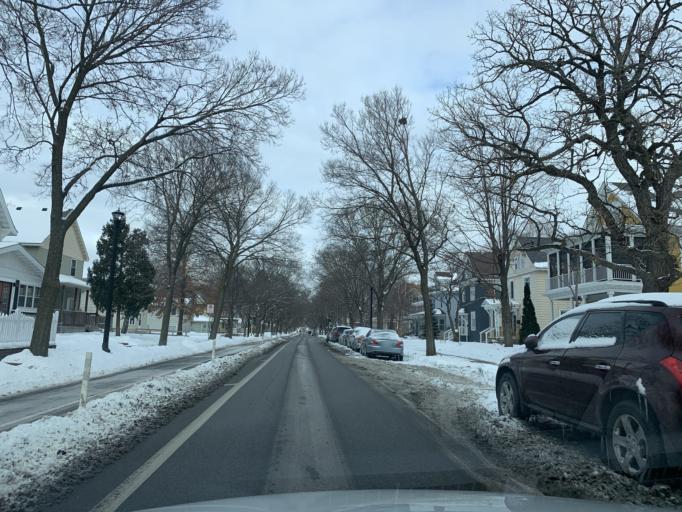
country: US
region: Minnesota
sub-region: Hennepin County
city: Minneapolis
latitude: 44.9942
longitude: -93.2941
